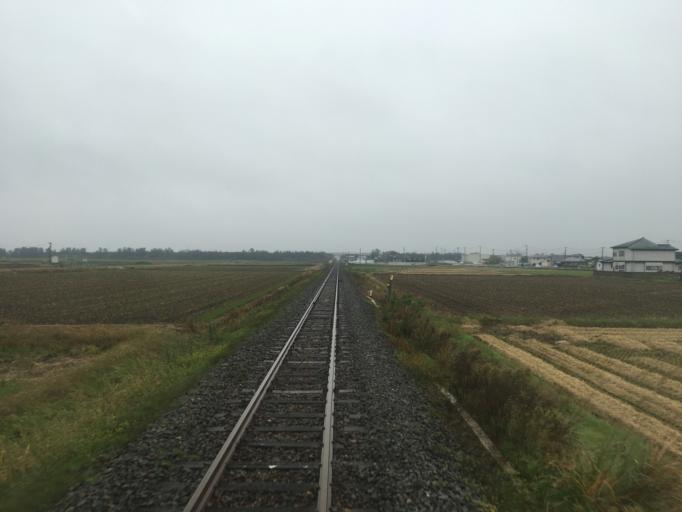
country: JP
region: Miyagi
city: Furukawa
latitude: 38.5736
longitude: 140.9193
